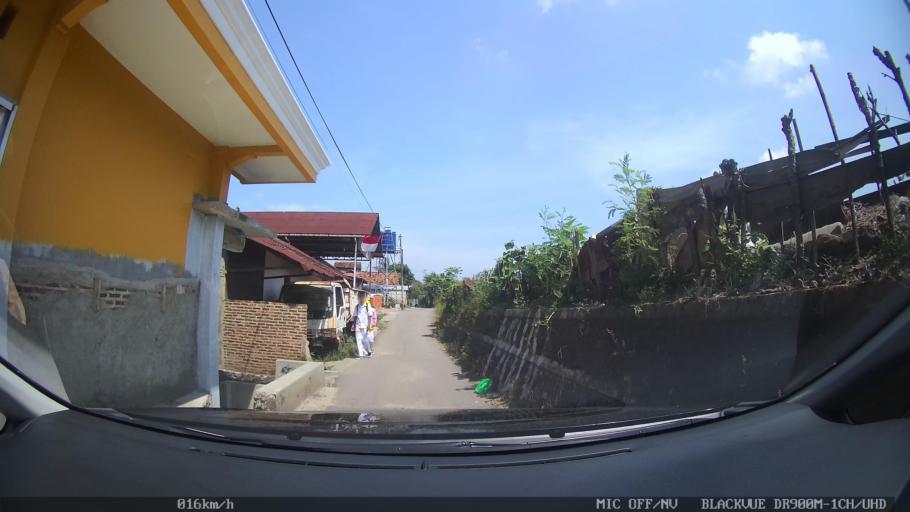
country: ID
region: Lampung
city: Kedaton
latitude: -5.3709
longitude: 105.2509
